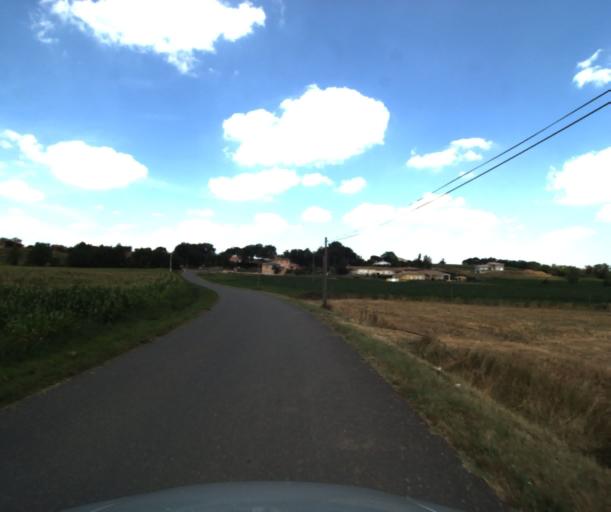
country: FR
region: Midi-Pyrenees
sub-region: Departement de la Haute-Garonne
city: Labastidette
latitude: 43.4603
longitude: 1.2181
